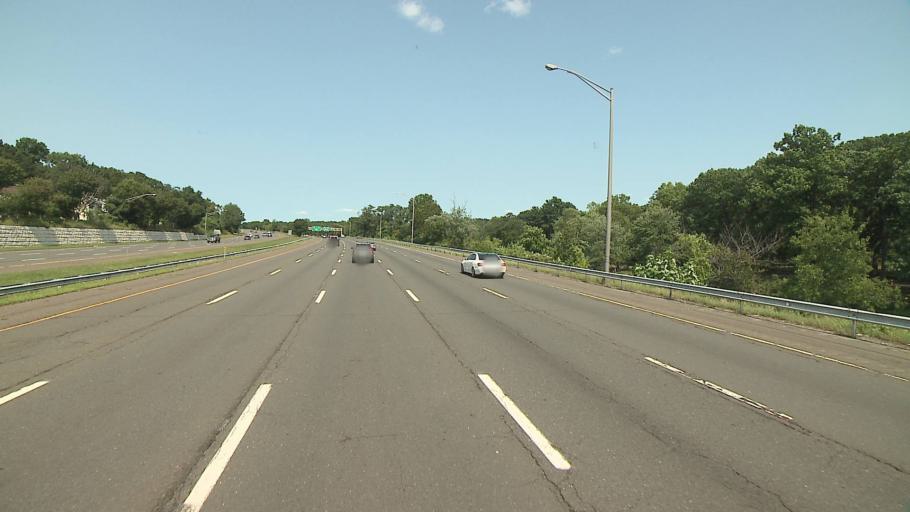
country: US
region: Connecticut
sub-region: Fairfield County
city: Trumbull
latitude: 41.2133
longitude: -73.1837
